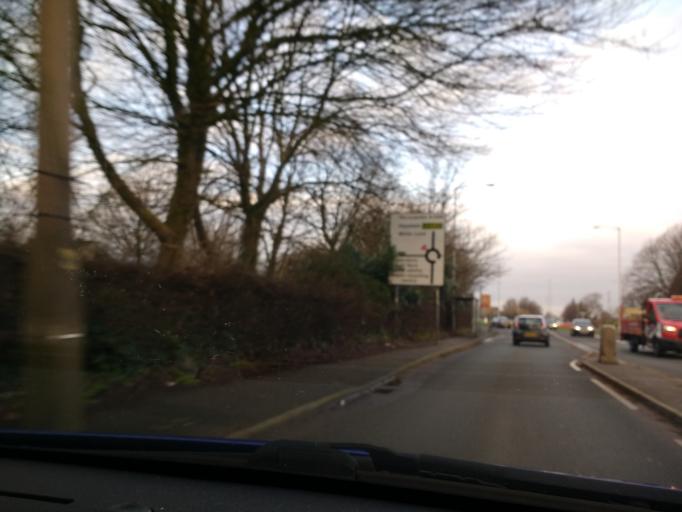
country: GB
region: England
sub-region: Lancashire
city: Lancaster
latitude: 54.0590
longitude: -2.8233
